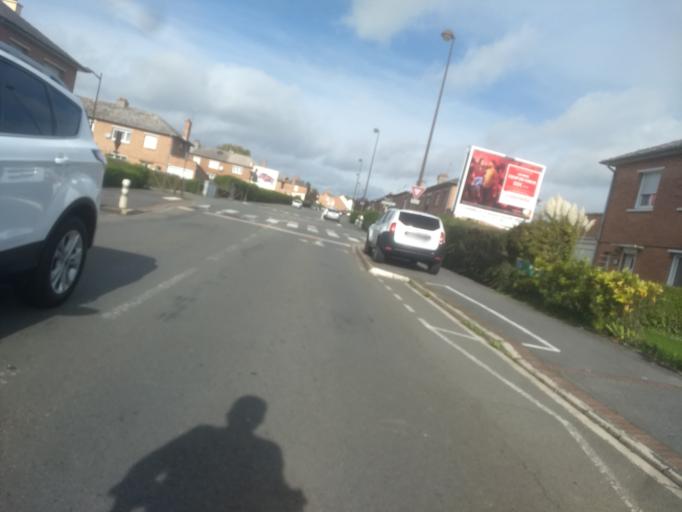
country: FR
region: Nord-Pas-de-Calais
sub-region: Departement du Pas-de-Calais
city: Dainville
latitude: 50.2887
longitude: 2.7432
